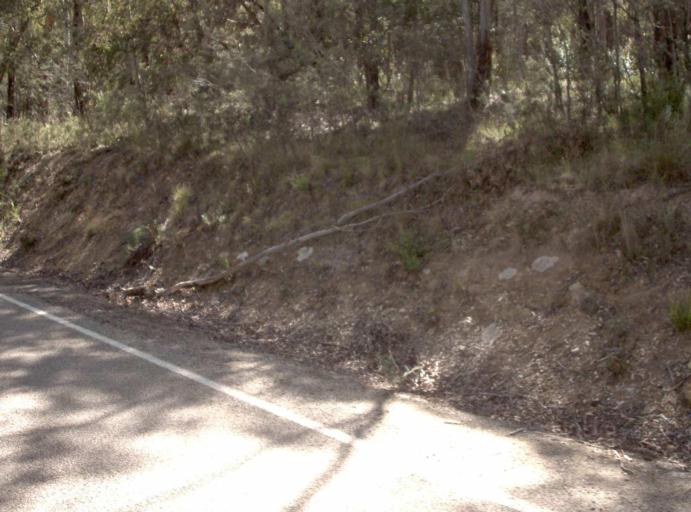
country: AU
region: New South Wales
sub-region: Bombala
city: Bombala
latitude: -37.1618
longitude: 148.7203
